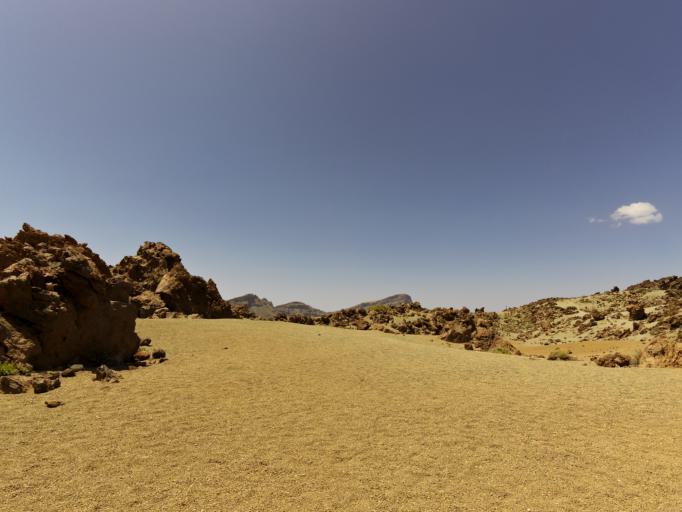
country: ES
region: Canary Islands
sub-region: Provincia de Santa Cruz de Tenerife
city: Los Realejos
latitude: 28.2651
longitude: -16.5871
